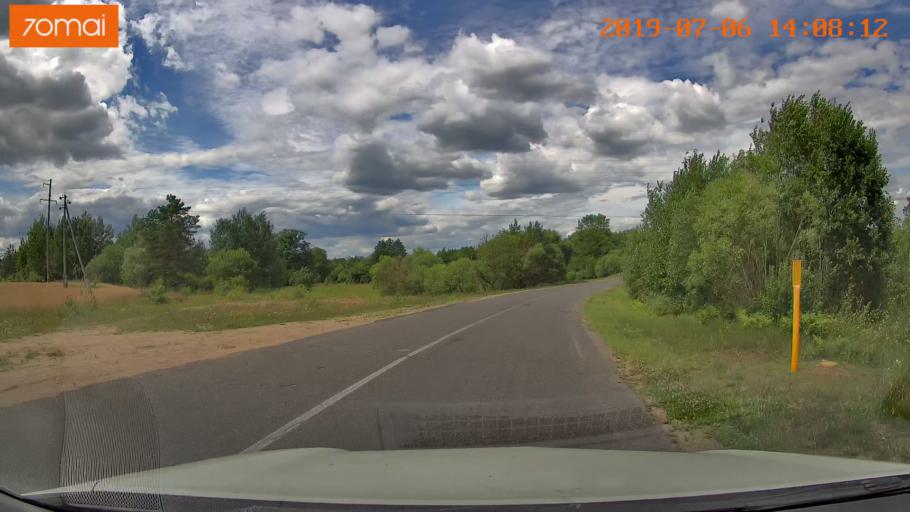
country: BY
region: Minsk
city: Ivyanyets
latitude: 53.8729
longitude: 26.7596
